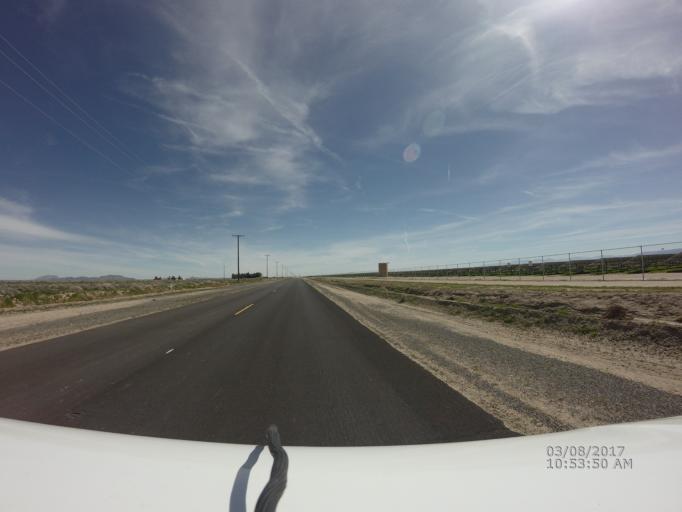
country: US
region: California
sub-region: Los Angeles County
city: Green Valley
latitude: 34.8193
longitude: -118.3880
